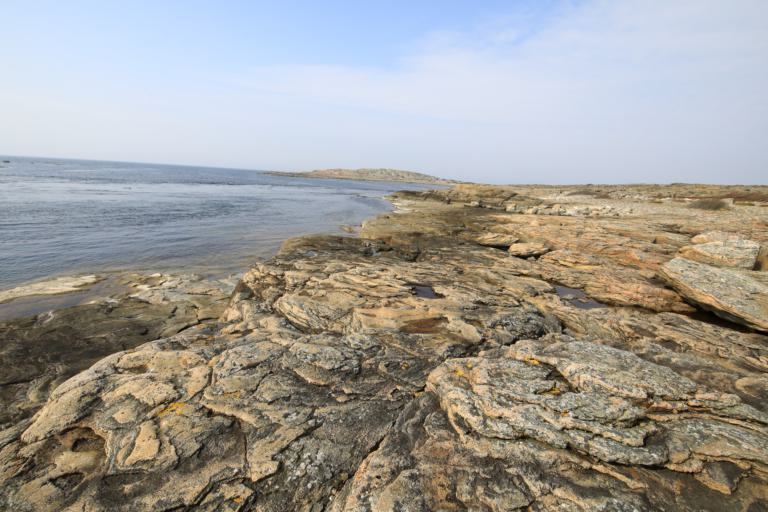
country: SE
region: Halland
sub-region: Kungsbacka Kommun
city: Frillesas
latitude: 57.2519
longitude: 12.0910
